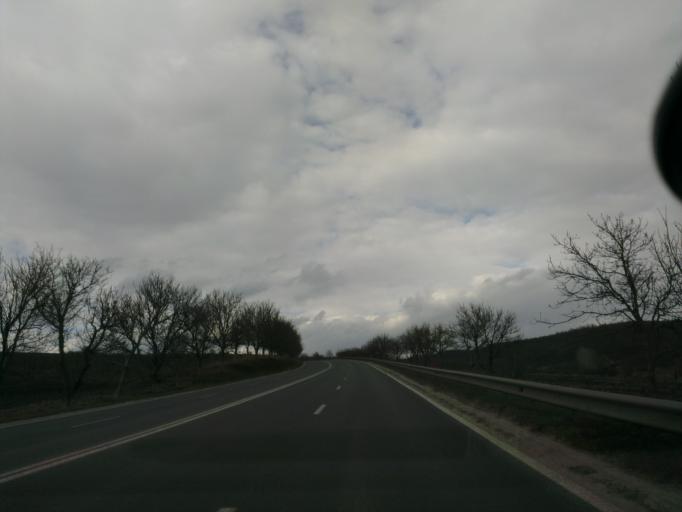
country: MD
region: Laloveni
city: Ialoveni
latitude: 46.9296
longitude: 28.6994
